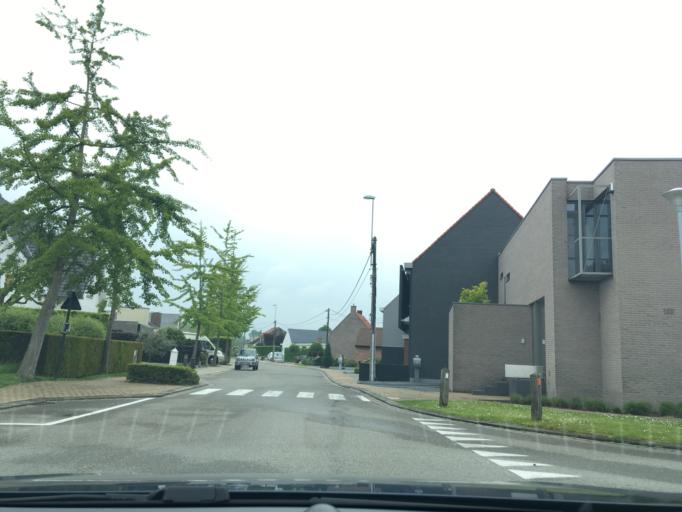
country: BE
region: Flanders
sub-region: Provincie West-Vlaanderen
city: Roeselare
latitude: 50.9284
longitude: 3.1626
